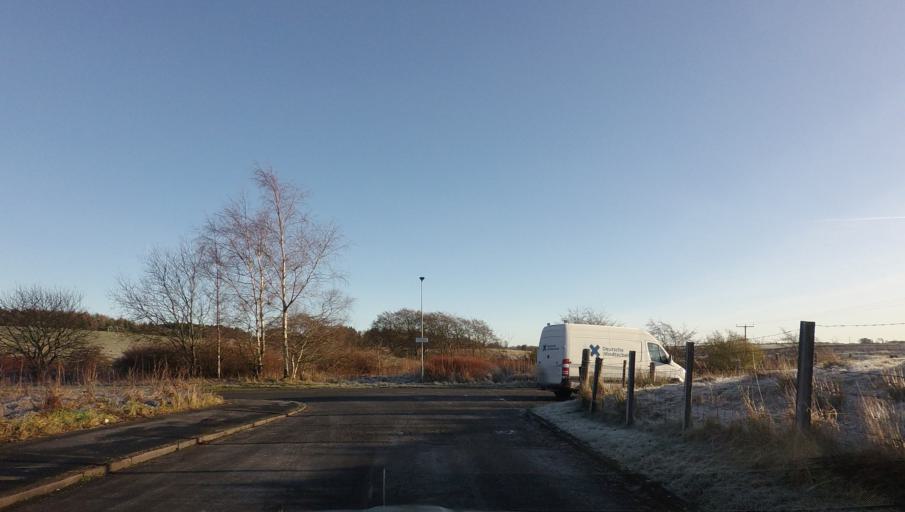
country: GB
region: Scotland
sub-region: North Lanarkshire
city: Shotts
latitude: 55.8098
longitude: -3.8359
